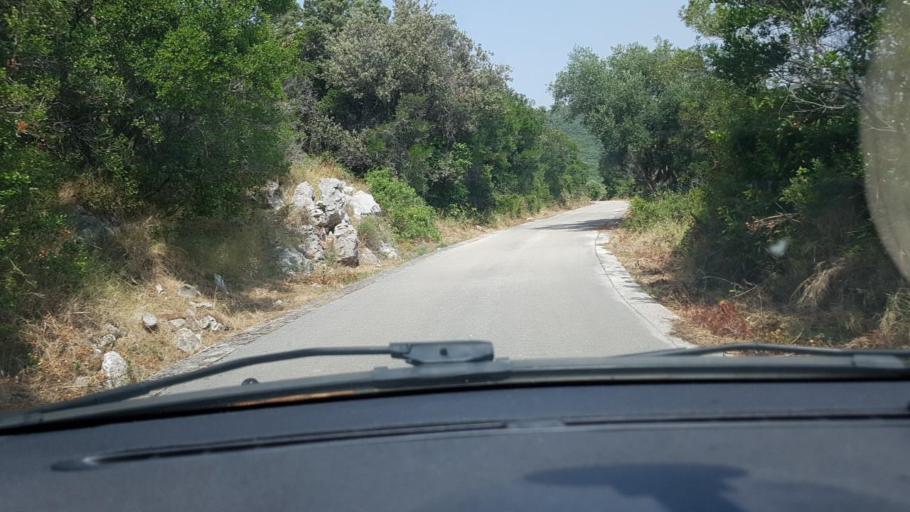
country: ME
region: Herceg Novi
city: Herceg-Novi
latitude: 42.4036
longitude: 18.5143
